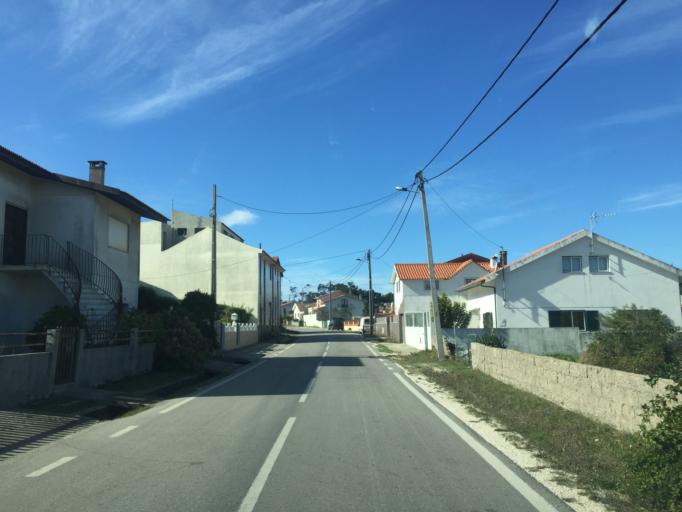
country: PT
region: Coimbra
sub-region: Figueira da Foz
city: Buarcos
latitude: 40.1911
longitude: -8.8661
